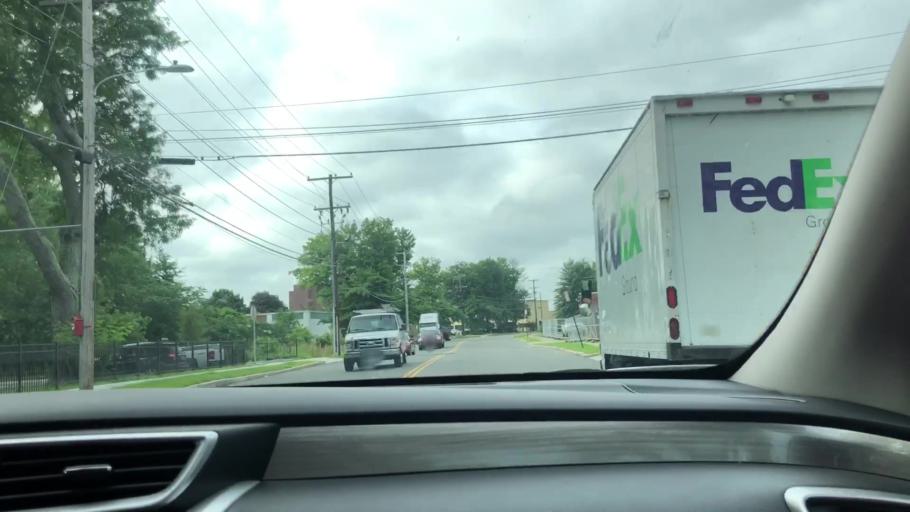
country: US
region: Rhode Island
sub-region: Providence County
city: Providence
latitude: 41.8435
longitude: -71.4123
